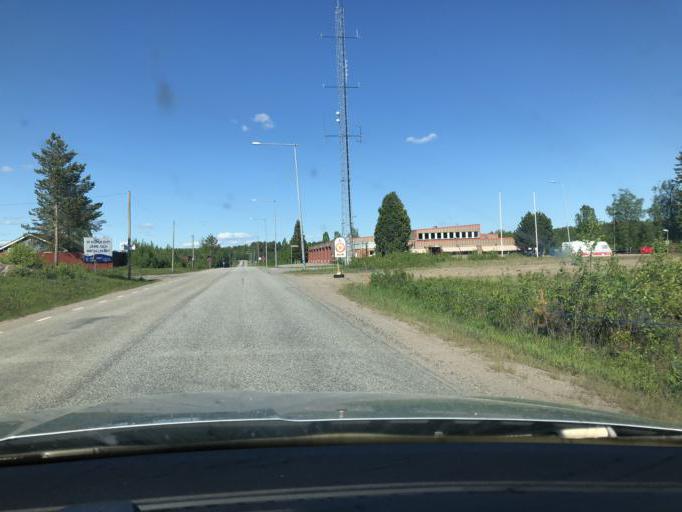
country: SE
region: Norrbotten
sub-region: Kalix Kommun
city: Kalix
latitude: 65.8690
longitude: 23.1454
